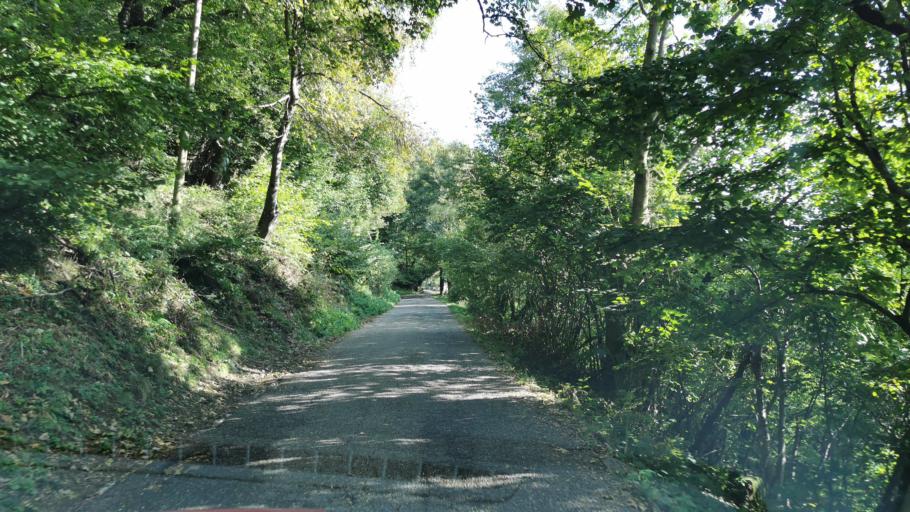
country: IT
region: Lombardy
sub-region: Provincia di Como
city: Moltrasio
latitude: 45.8711
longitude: 9.0762
